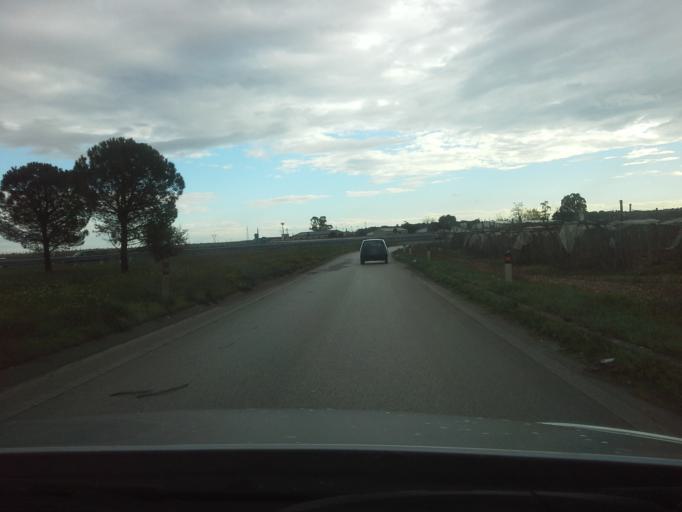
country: IT
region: Apulia
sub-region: Provincia di Bari
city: Cellamare
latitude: 41.0007
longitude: 16.9125
